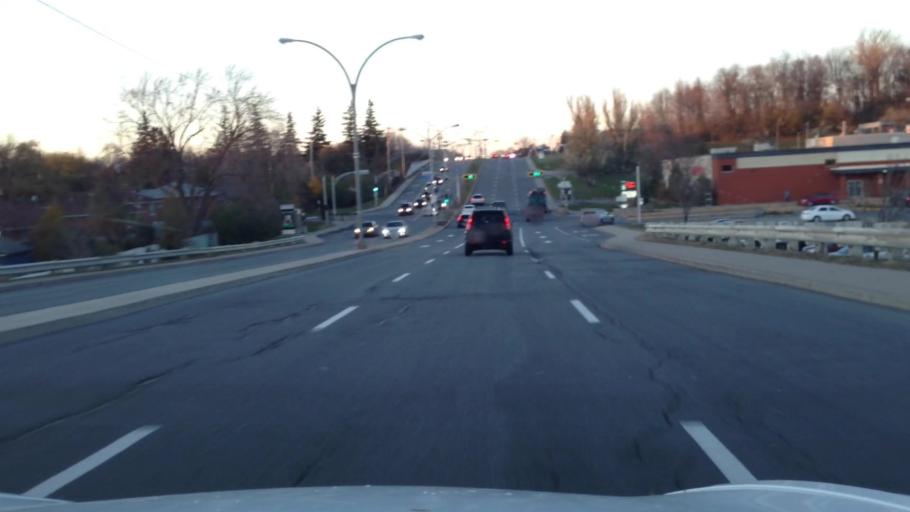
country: CA
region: Quebec
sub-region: Montreal
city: Pointe-Claire
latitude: 45.4446
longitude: -73.8160
